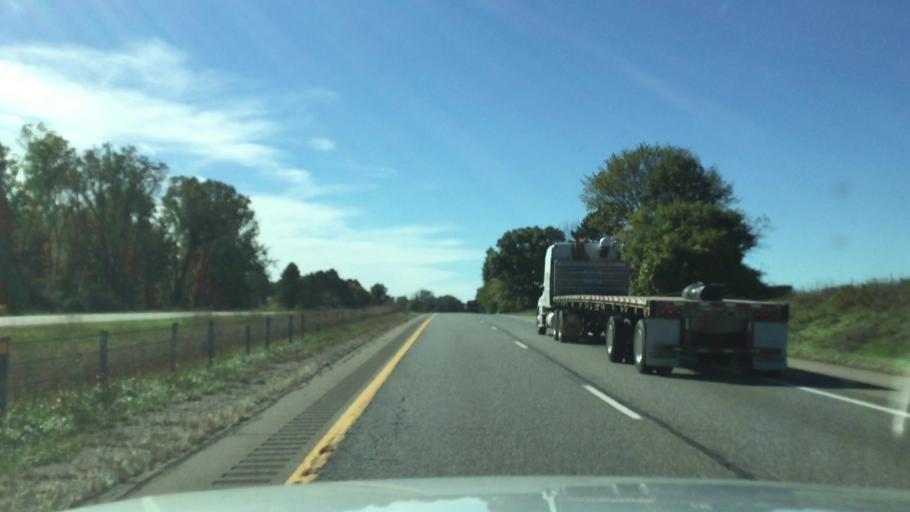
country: US
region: Michigan
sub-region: Jackson County
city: Grass Lake
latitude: 42.2973
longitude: -84.1253
